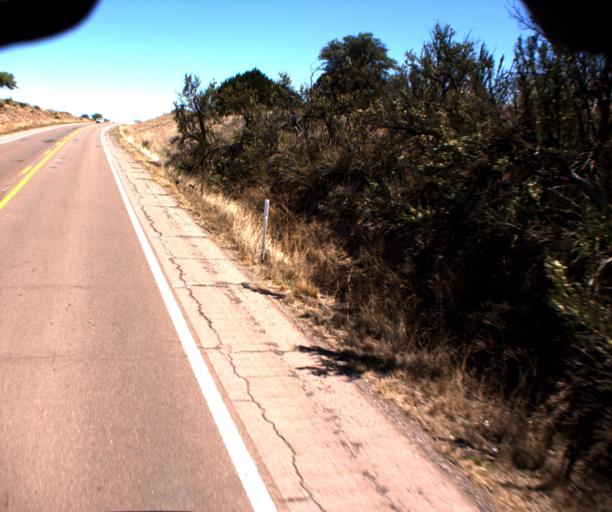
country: US
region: Arizona
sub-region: Pima County
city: Corona de Tucson
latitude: 31.6743
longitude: -110.6690
